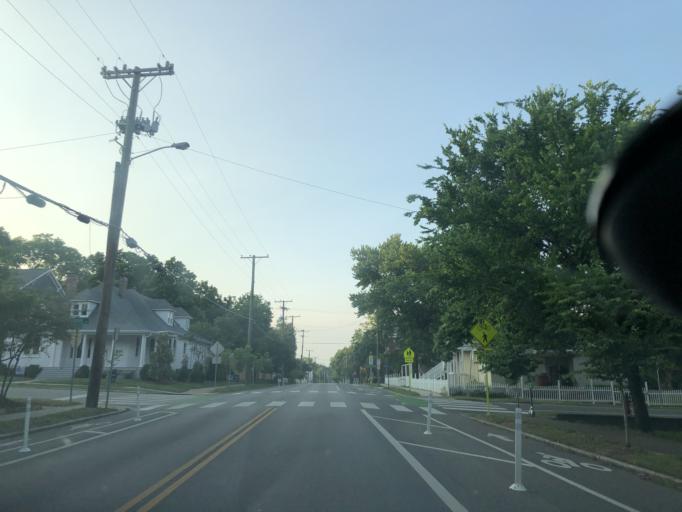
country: US
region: Tennessee
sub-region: Davidson County
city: Oak Hill
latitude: 36.1242
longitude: -86.7864
